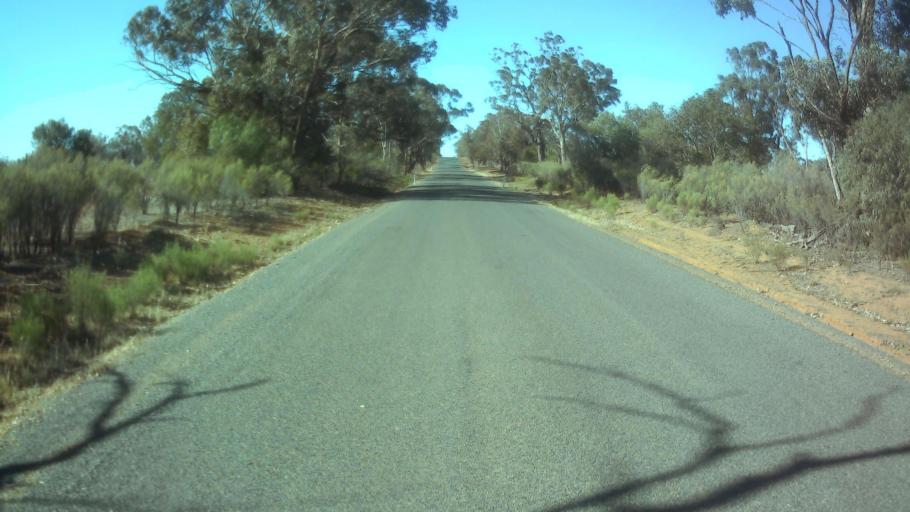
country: AU
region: New South Wales
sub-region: Forbes
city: Forbes
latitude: -33.7083
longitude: 147.8052
